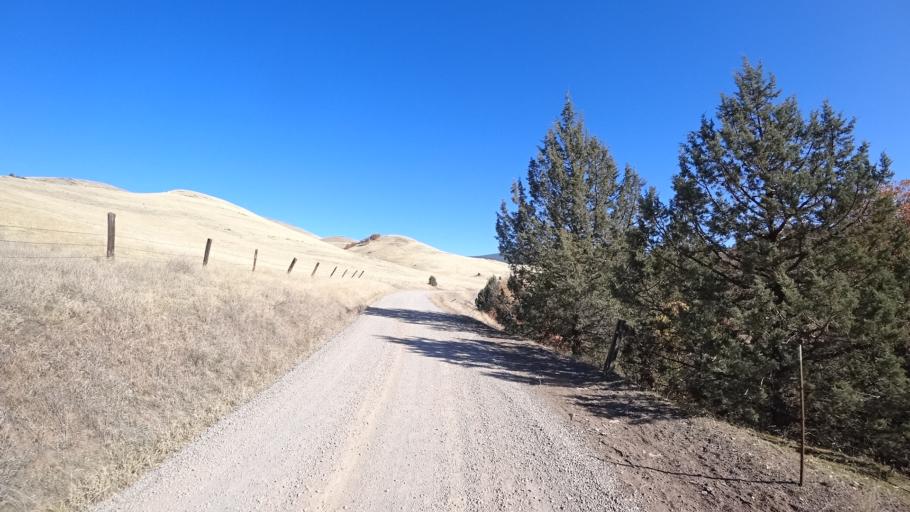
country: US
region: California
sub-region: Siskiyou County
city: Montague
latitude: 41.7929
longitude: -122.3491
